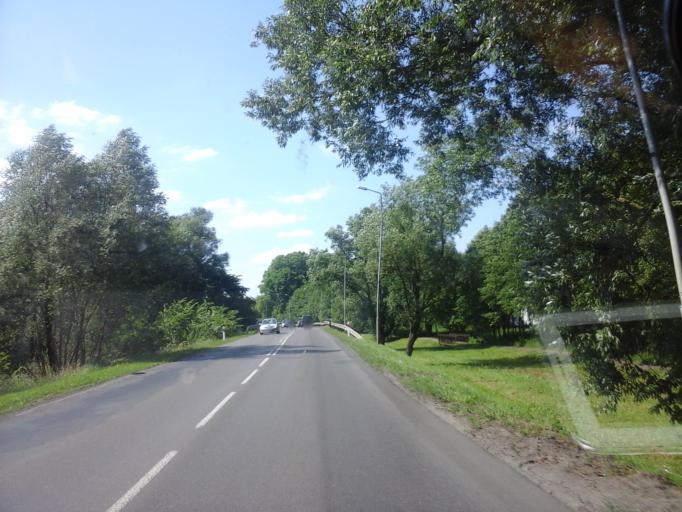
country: PL
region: West Pomeranian Voivodeship
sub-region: Powiat bialogardzki
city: Bialogard
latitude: 54.0016
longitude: 15.9876
